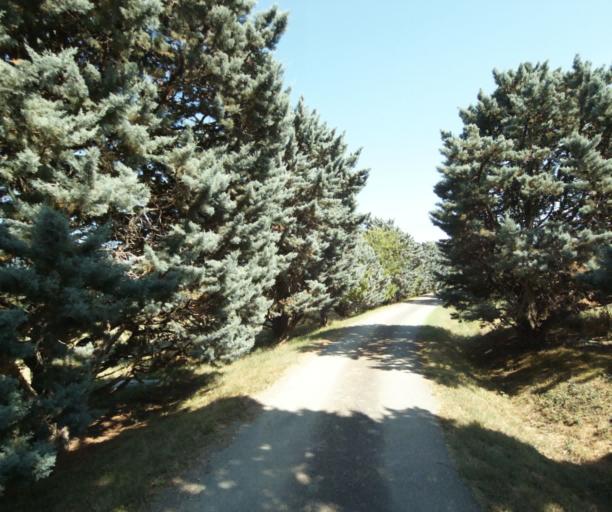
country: FR
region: Midi-Pyrenees
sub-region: Departement de la Haute-Garonne
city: Saint-Felix-Lauragais
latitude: 43.4782
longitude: 1.8878
